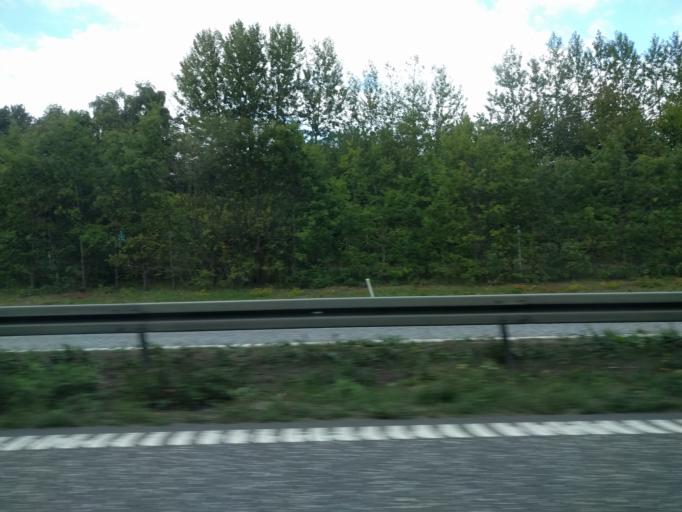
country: DK
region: South Denmark
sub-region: Assens Kommune
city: Tommerup Stationsby
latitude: 55.3869
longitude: 10.2155
